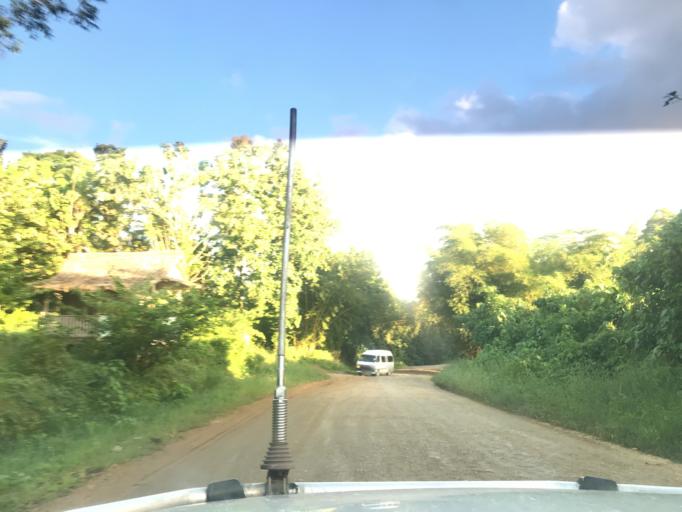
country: SB
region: Malaita
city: Auki
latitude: -8.7101
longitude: 160.7036
